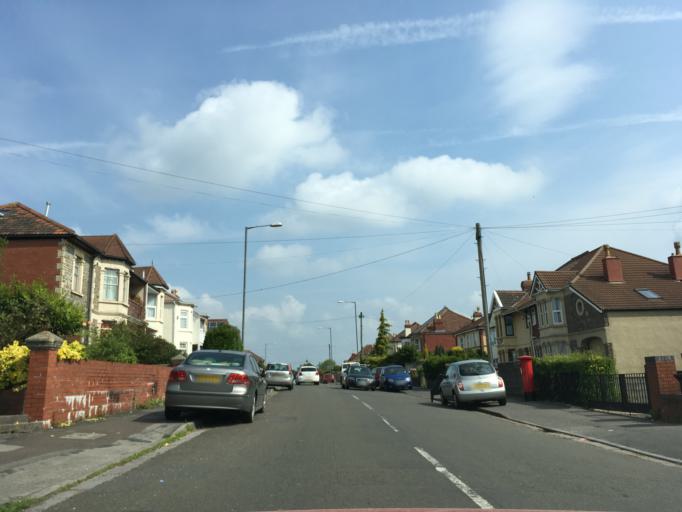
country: GB
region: England
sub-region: North Somerset
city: Dundry
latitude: 51.4124
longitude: -2.6193
